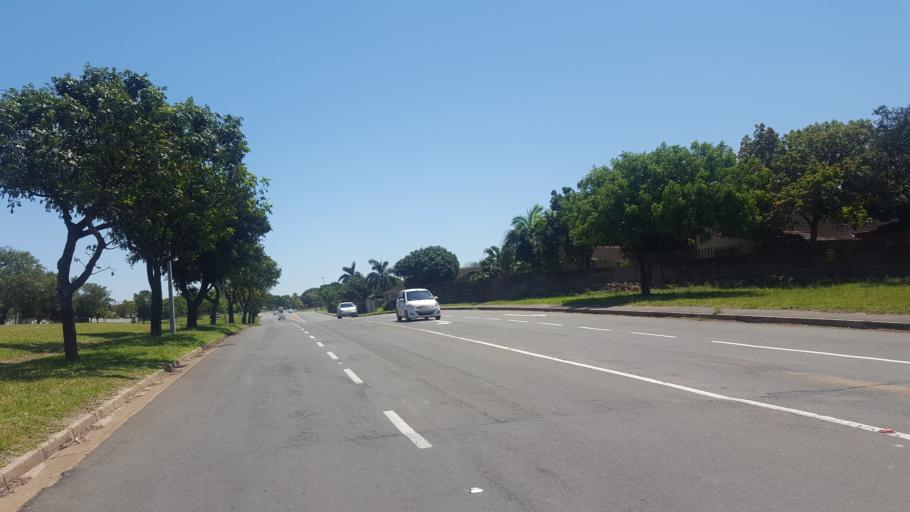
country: ZA
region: KwaZulu-Natal
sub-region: uThungulu District Municipality
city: Richards Bay
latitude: -28.7611
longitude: 32.0618
